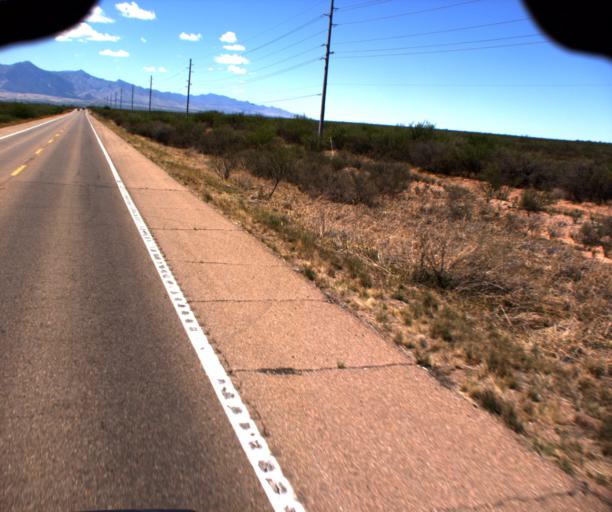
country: US
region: Arizona
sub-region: Cochise County
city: Naco
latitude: 31.3757
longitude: -110.0059
